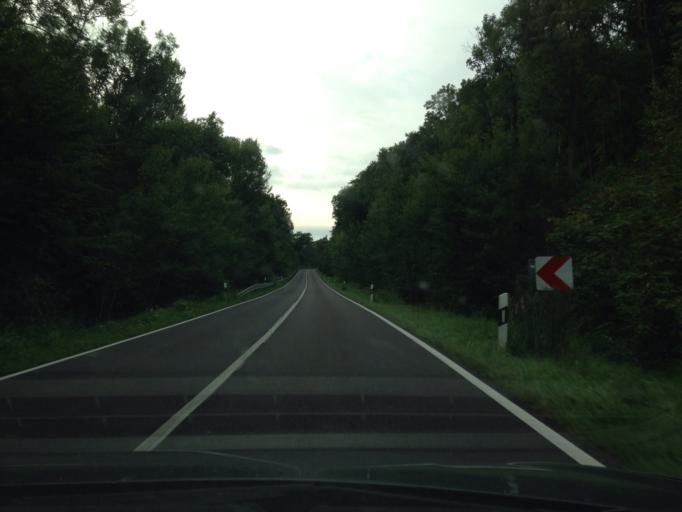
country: DE
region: Mecklenburg-Vorpommern
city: Loitz
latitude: 53.3480
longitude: 13.4123
